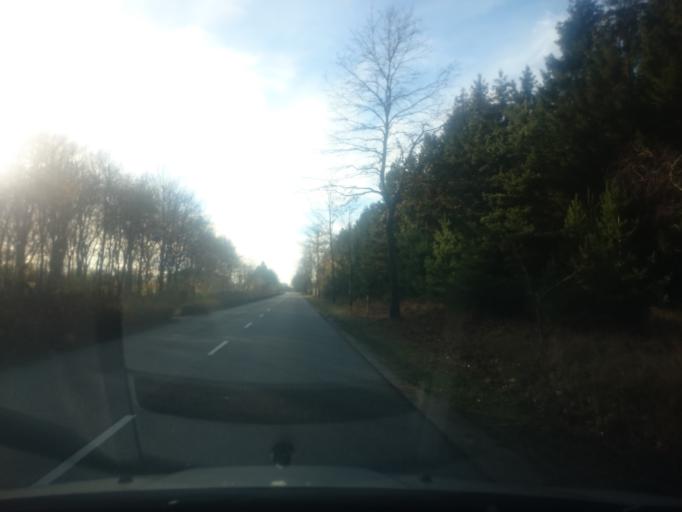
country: DK
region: South Denmark
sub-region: Billund Kommune
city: Billund
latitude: 55.7386
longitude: 9.1132
